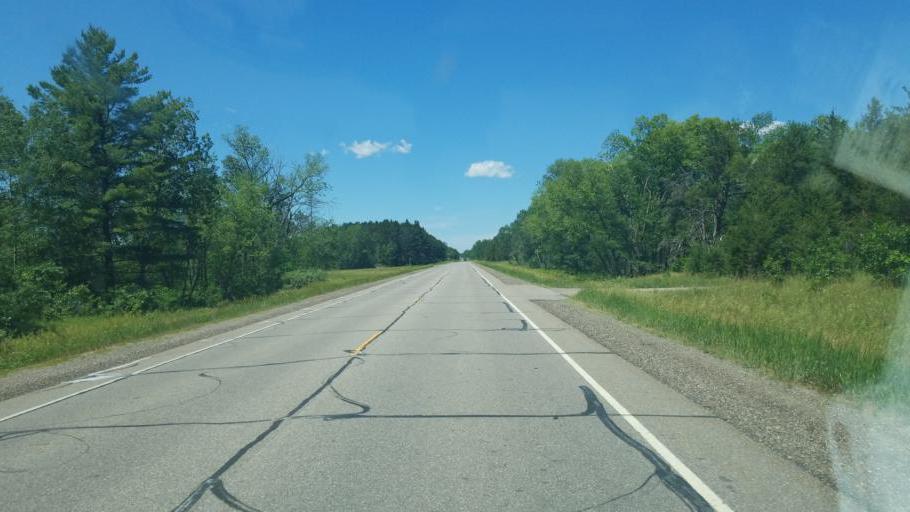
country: US
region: Wisconsin
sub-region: Adams County
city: Friendship
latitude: 44.0468
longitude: -89.9929
